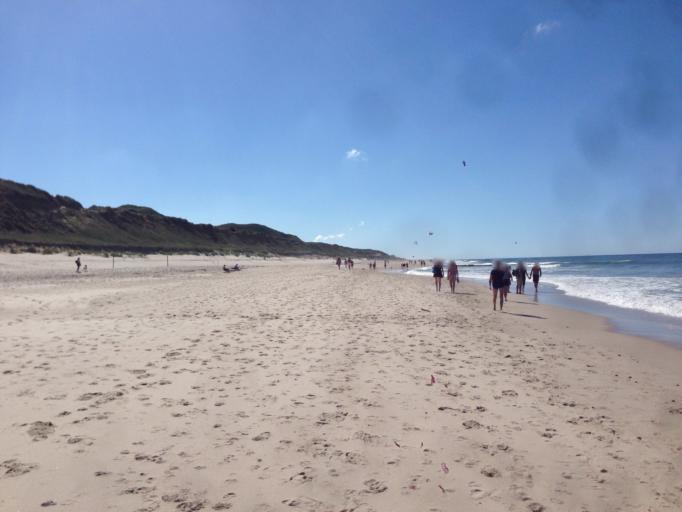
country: DE
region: Schleswig-Holstein
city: Westerland
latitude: 54.9532
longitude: 8.3244
